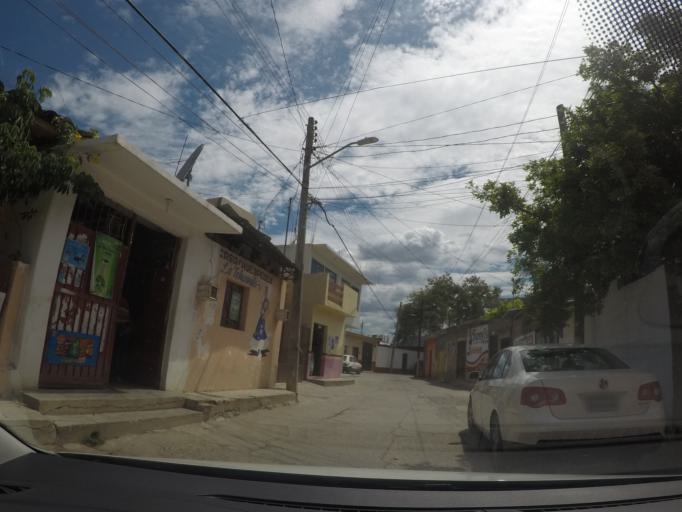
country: MX
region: Oaxaca
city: San Blas Atempa
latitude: 16.3354
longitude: -95.2285
